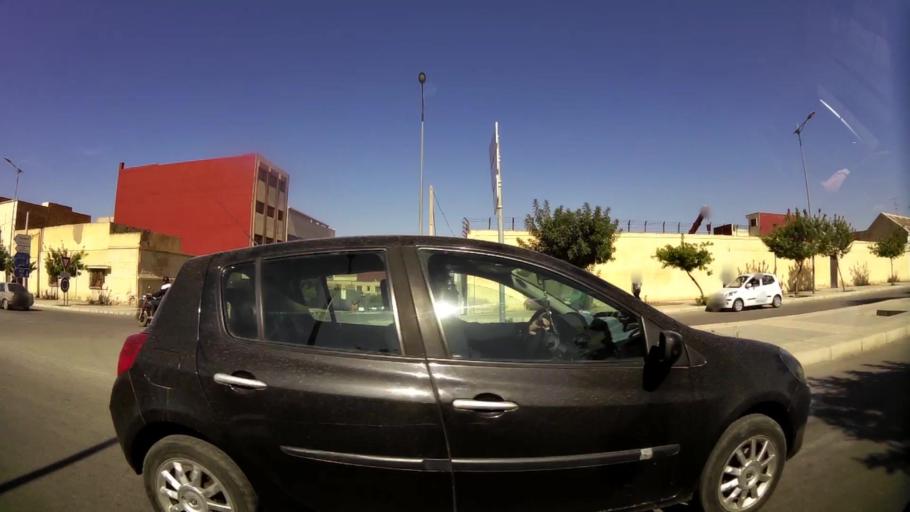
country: MA
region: Oriental
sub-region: Oujda-Angad
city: Oujda
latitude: 34.6921
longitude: -1.9214
